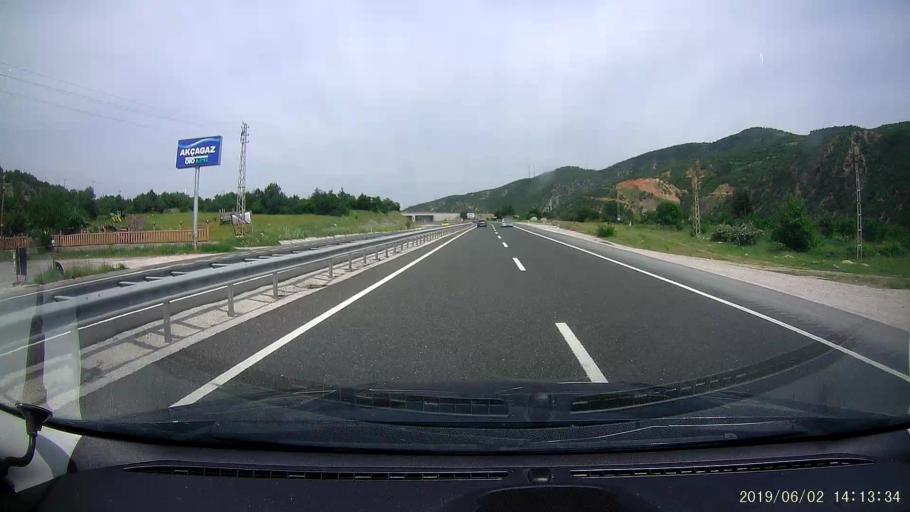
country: TR
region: Cankiri
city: Yaprakli
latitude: 40.9266
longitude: 33.8333
